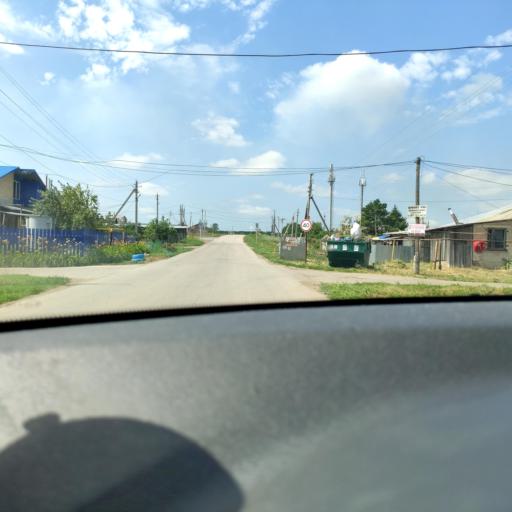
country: RU
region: Samara
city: Kinel'
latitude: 53.3443
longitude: 50.5202
